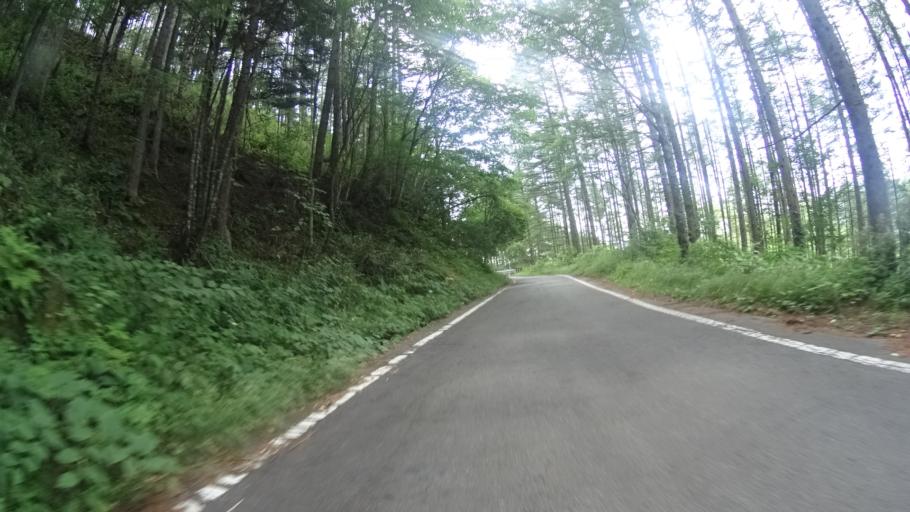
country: JP
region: Yamanashi
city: Enzan
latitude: 35.8360
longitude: 138.6411
